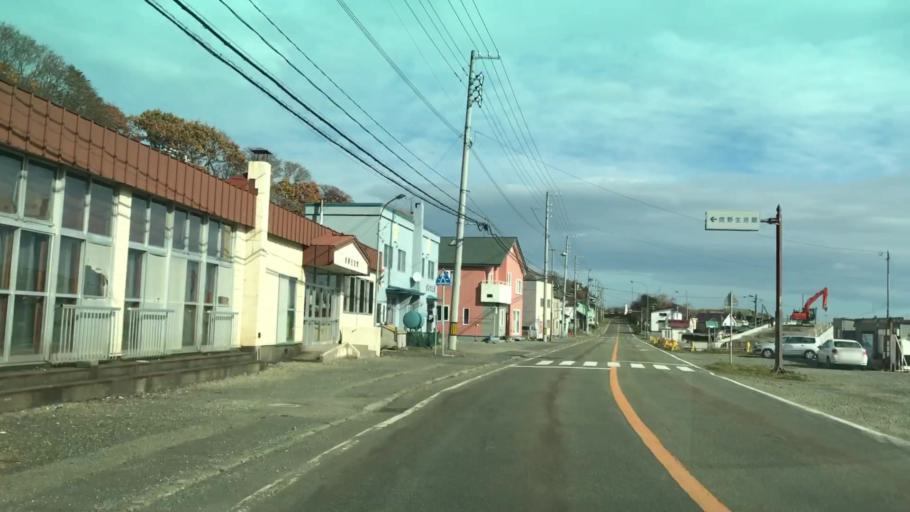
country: JP
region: Hokkaido
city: Obihiro
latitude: 42.0435
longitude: 143.2940
